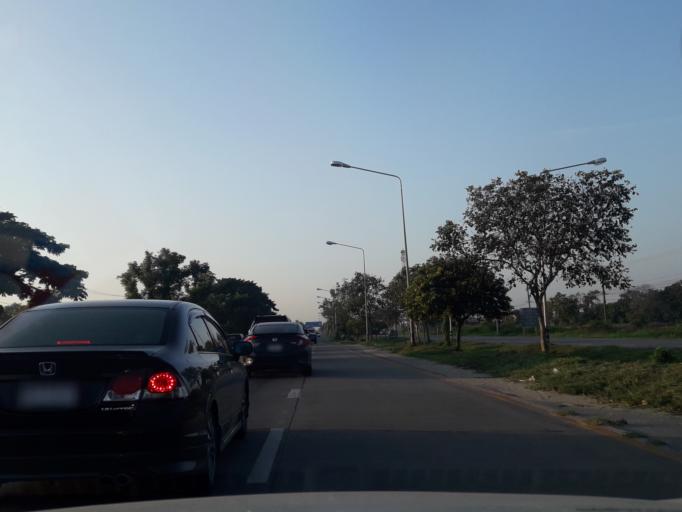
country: TH
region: Phra Nakhon Si Ayutthaya
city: Phra Nakhon Si Ayutthaya
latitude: 14.3487
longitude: 100.5284
